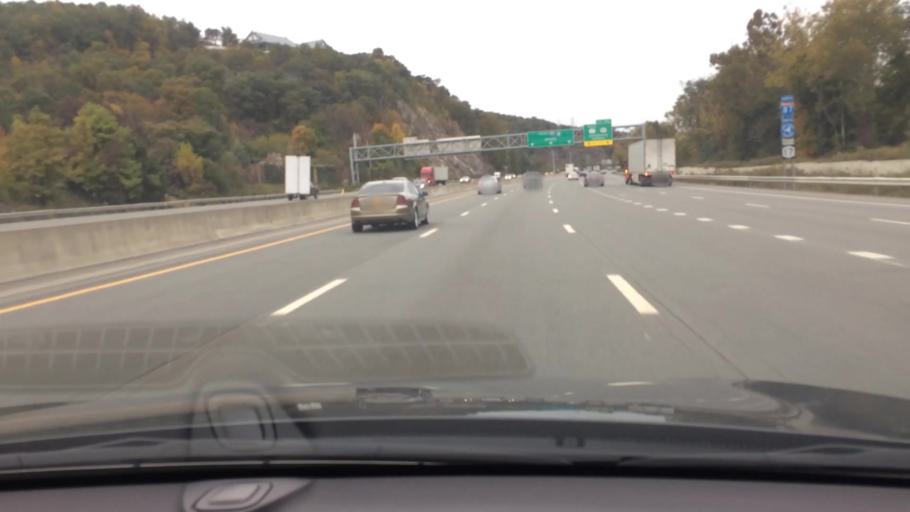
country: US
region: New York
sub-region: Rockland County
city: Suffern
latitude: 41.1255
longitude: -74.1657
